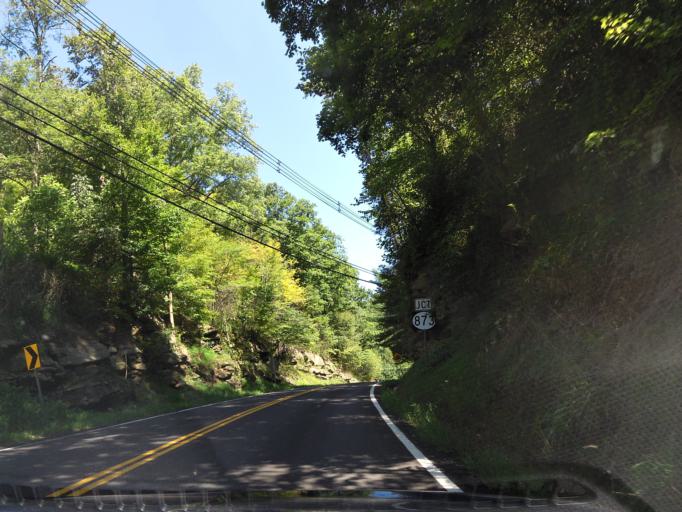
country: US
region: Kentucky
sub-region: Clay County
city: Manchester
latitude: 37.1050
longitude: -83.6636
